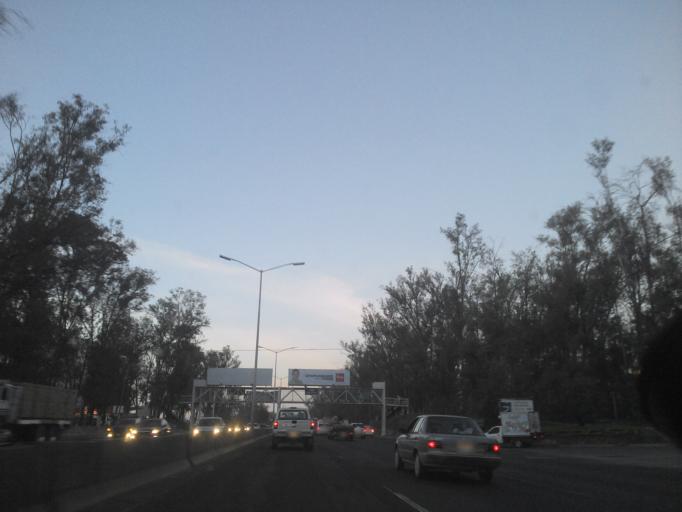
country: MX
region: Jalisco
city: Zapopan2
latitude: 20.6831
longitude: -103.4553
